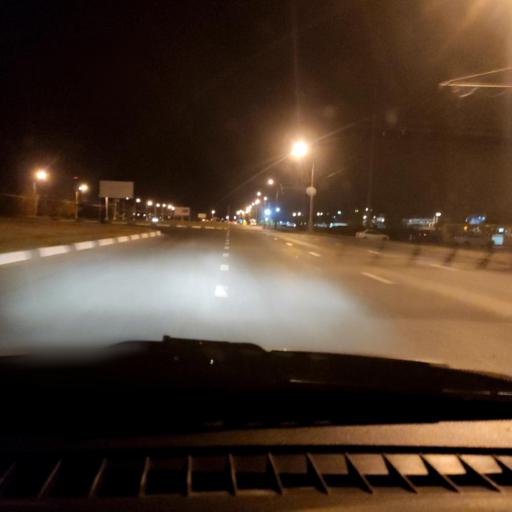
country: RU
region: Samara
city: Podstepki
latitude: 53.5581
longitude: 49.2333
